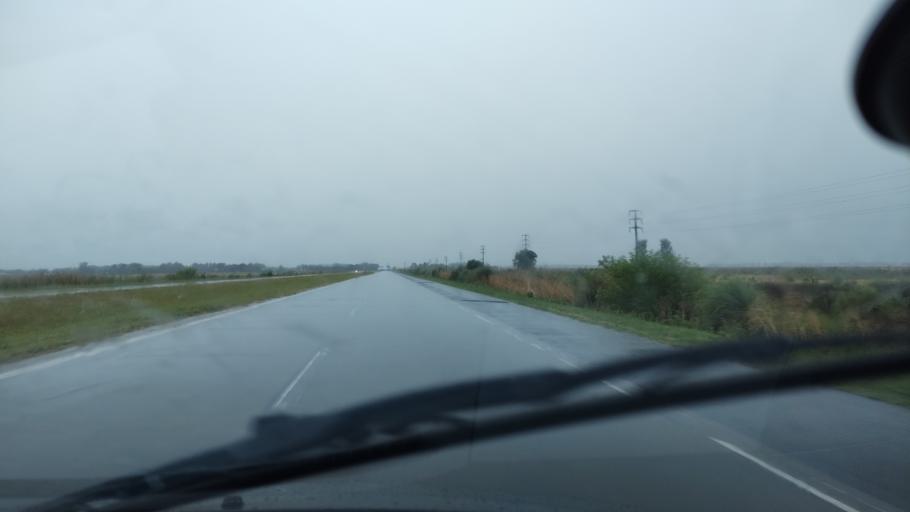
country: AR
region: Buenos Aires
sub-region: Partido de San Vicente
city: San Vicente
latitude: -35.0628
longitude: -58.4651
